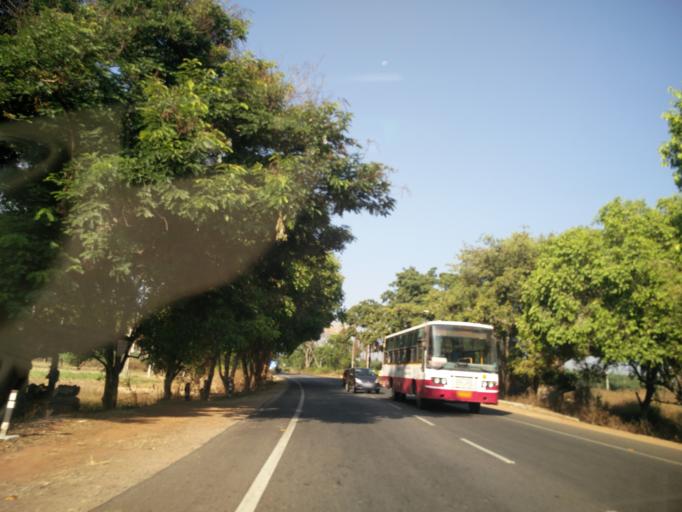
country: IN
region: Karnataka
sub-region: Tumkur
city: Gubbi
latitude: 13.3310
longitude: 76.9713
